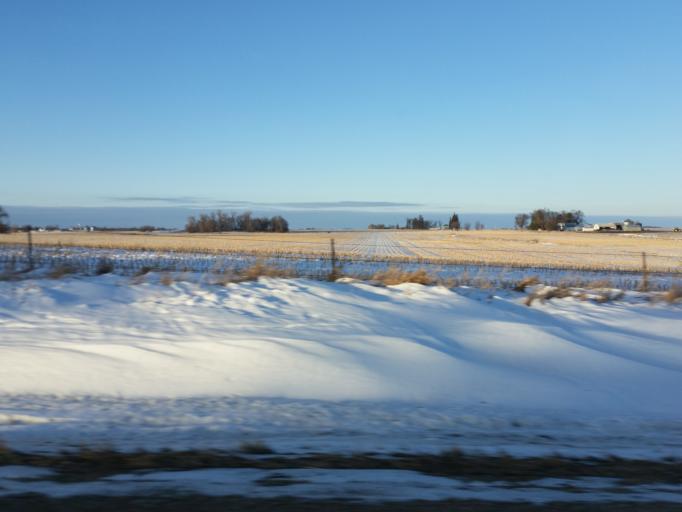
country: US
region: Iowa
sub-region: Butler County
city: Allison
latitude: 42.7450
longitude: -92.8905
